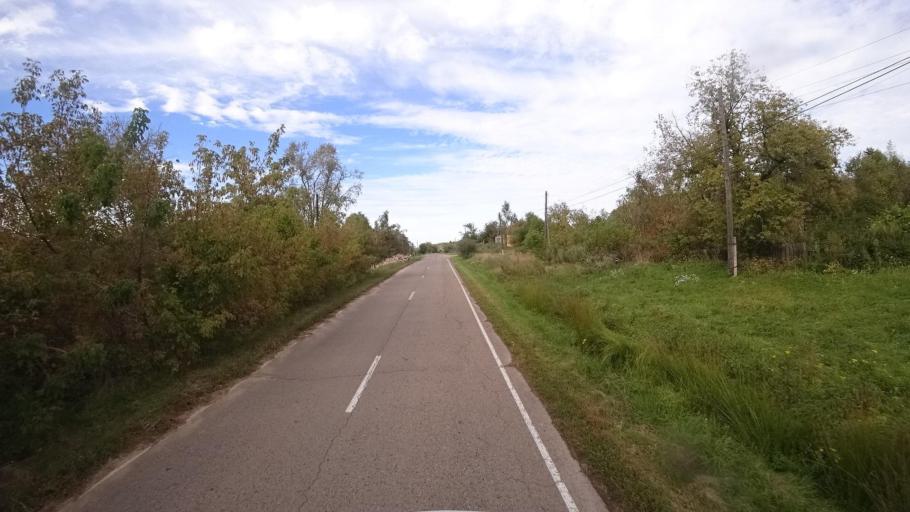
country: RU
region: Primorskiy
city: Dostoyevka
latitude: 44.3254
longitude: 133.4768
